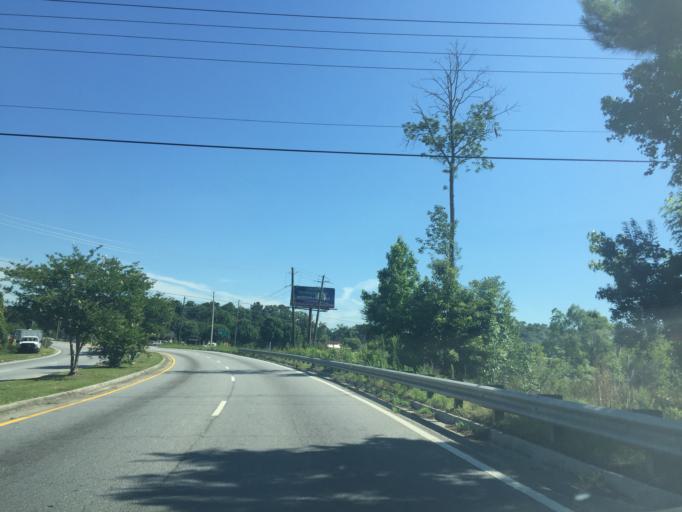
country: US
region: Georgia
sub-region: Chatham County
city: Garden City
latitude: 32.0469
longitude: -81.1653
